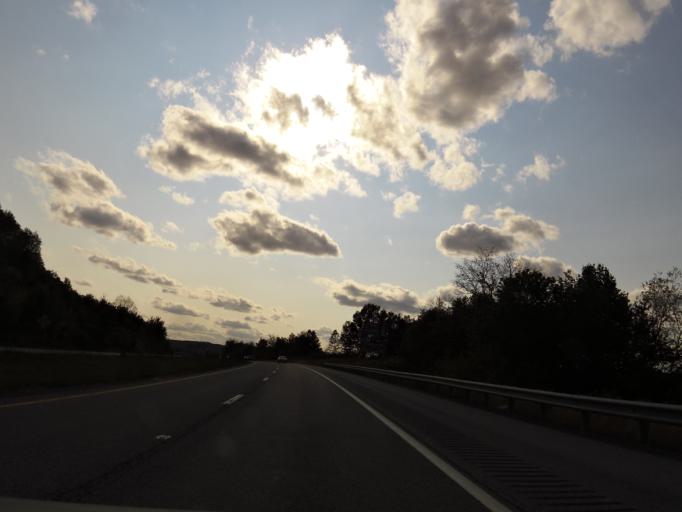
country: US
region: West Virginia
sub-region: Mercer County
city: Princeton
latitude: 37.3627
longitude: -81.0708
